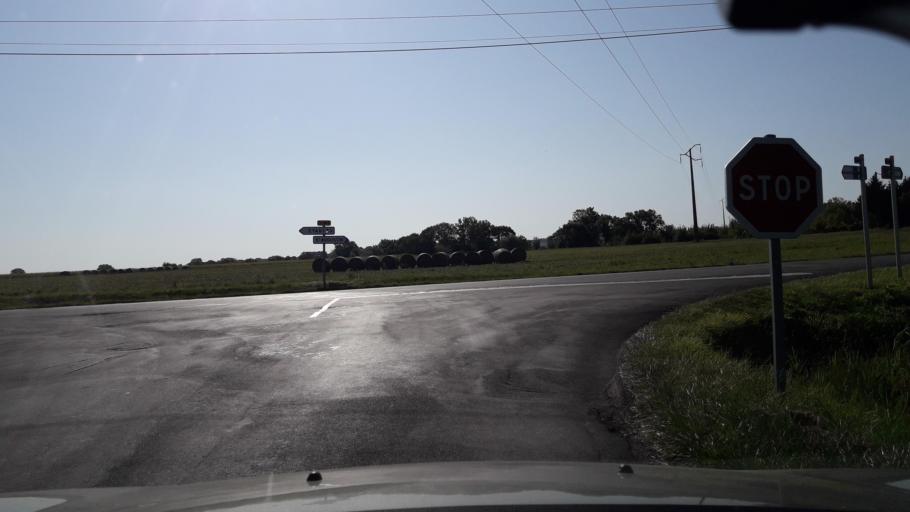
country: FR
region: Poitou-Charentes
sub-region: Departement de la Charente-Maritime
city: Etaules
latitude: 45.7096
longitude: -1.1134
